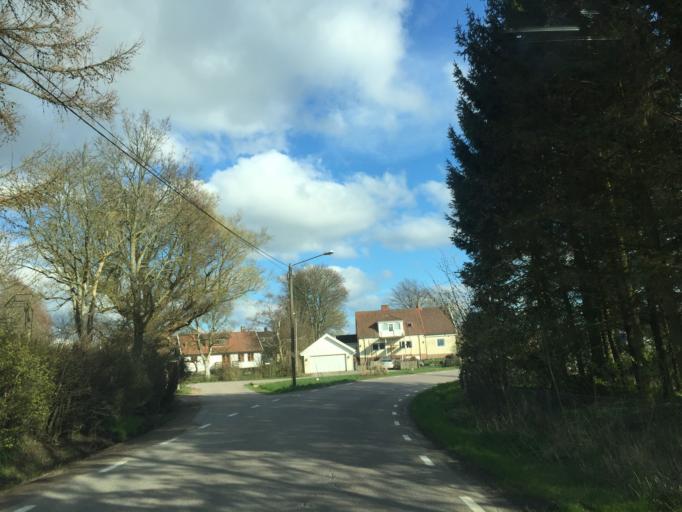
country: SE
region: Skane
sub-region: Skurups Kommun
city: Rydsgard
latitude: 55.4542
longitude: 13.6201
